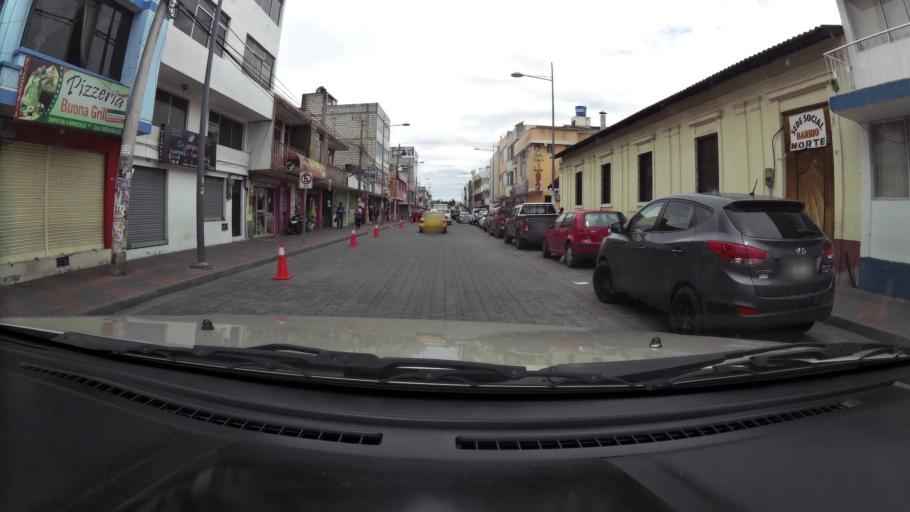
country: EC
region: Cotopaxi
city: San Miguel de Salcedo
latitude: -1.0207
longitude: -78.5918
